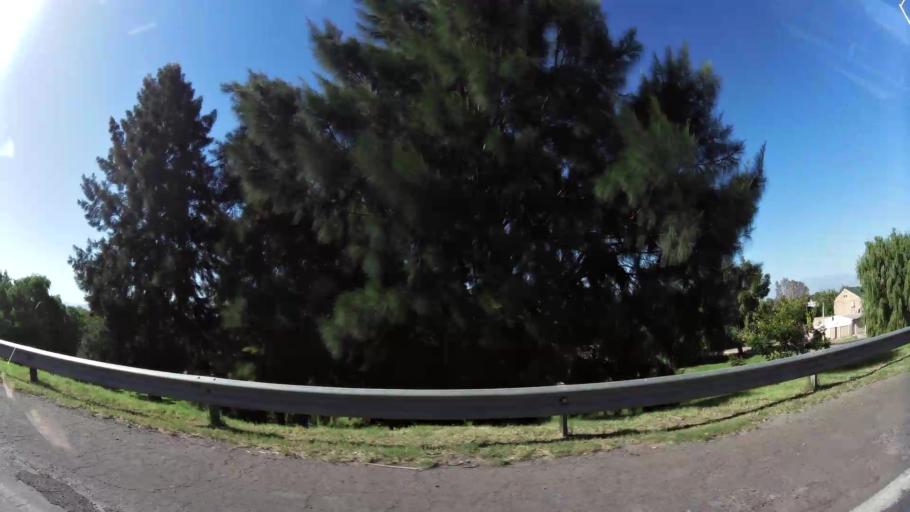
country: AR
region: San Juan
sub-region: Departamento de Santa Lucia
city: Santa Lucia
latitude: -31.5170
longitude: -68.5090
